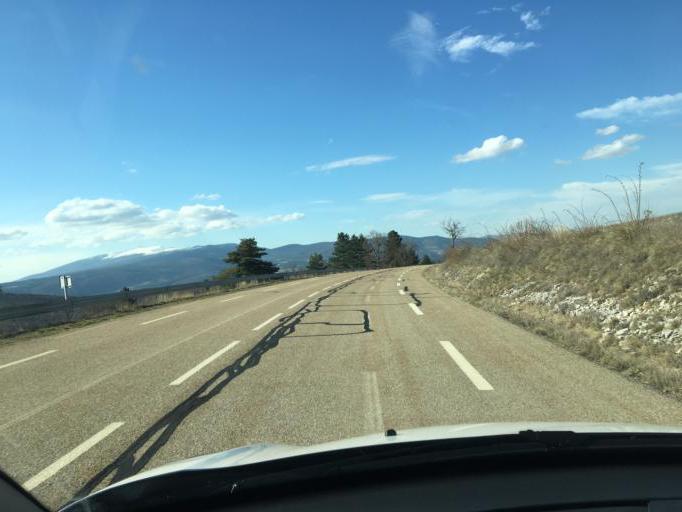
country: FR
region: Provence-Alpes-Cote d'Azur
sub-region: Departement du Vaucluse
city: Sault
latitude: 44.0489
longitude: 5.4421
